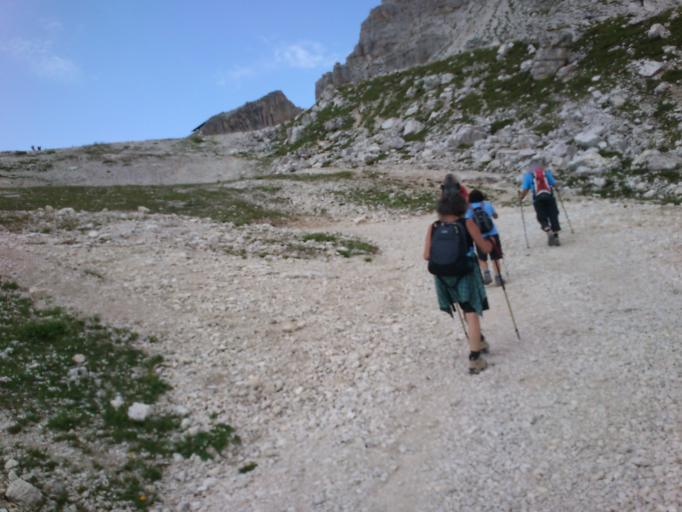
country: IT
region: Veneto
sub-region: Provincia di Belluno
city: Selva di Cadore
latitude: 46.5027
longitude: 12.0431
